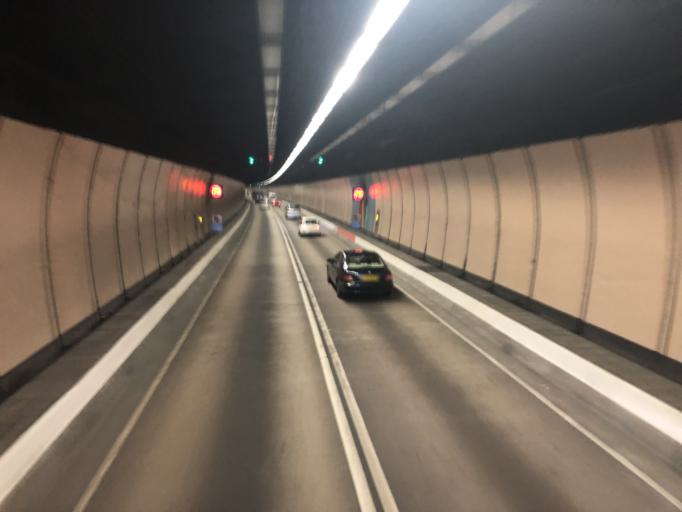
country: HK
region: Wong Tai Sin
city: Wong Tai Sin
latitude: 22.3431
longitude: 114.2052
